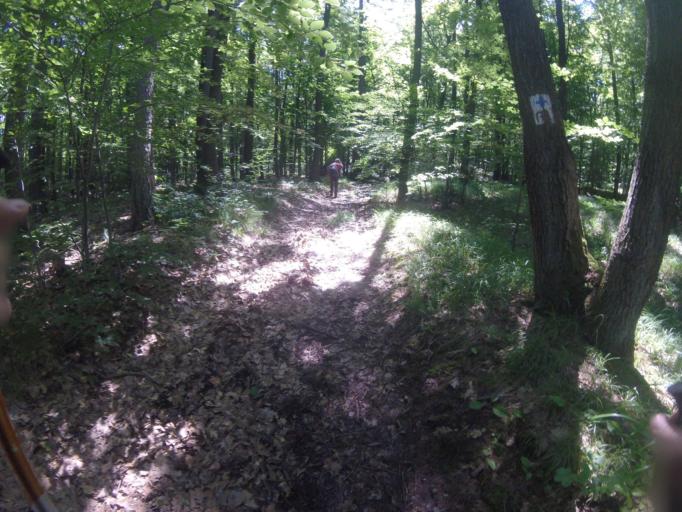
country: HU
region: Nograd
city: Batonyterenye
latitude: 47.9256
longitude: 19.8120
